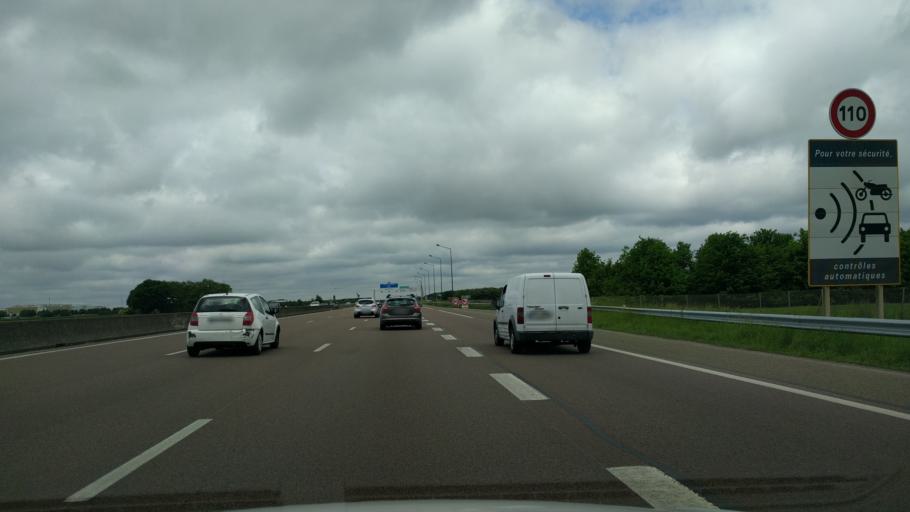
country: FR
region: Ile-de-France
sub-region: Departement de Seine-et-Marne
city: Lieusaint
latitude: 48.6141
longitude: 2.5650
